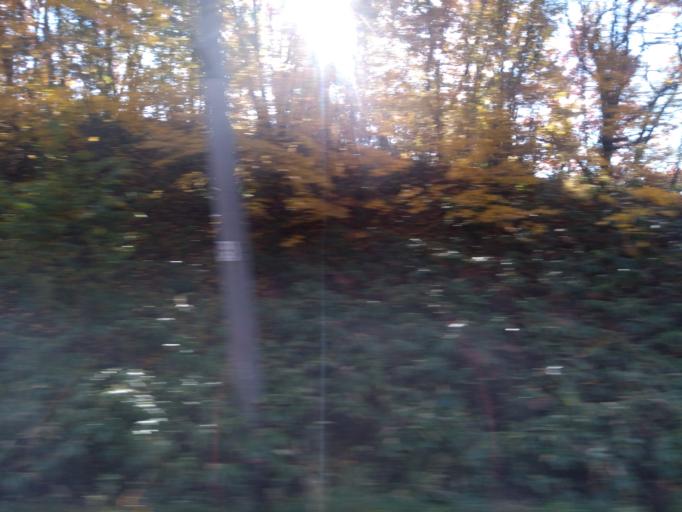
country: JP
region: Hokkaido
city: Kitahiroshima
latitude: 42.9961
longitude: 141.5373
